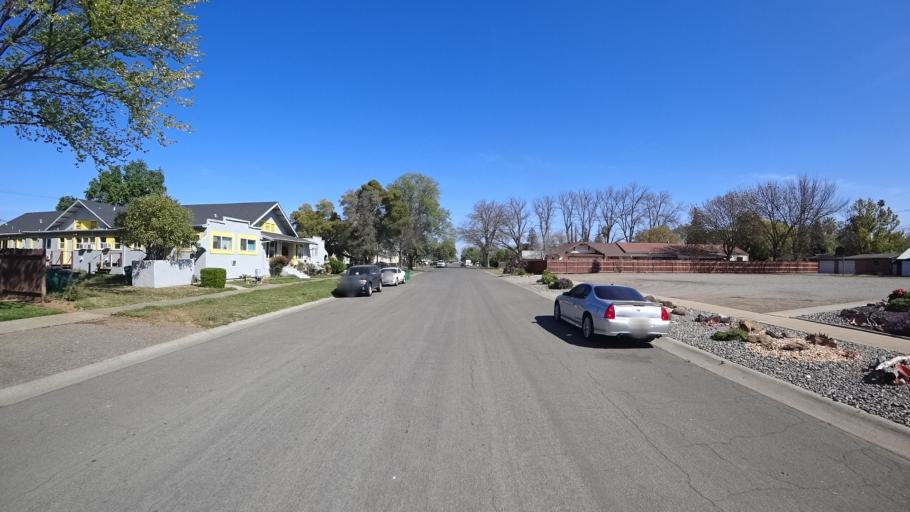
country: US
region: California
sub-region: Glenn County
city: Willows
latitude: 39.5211
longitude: -122.1908
